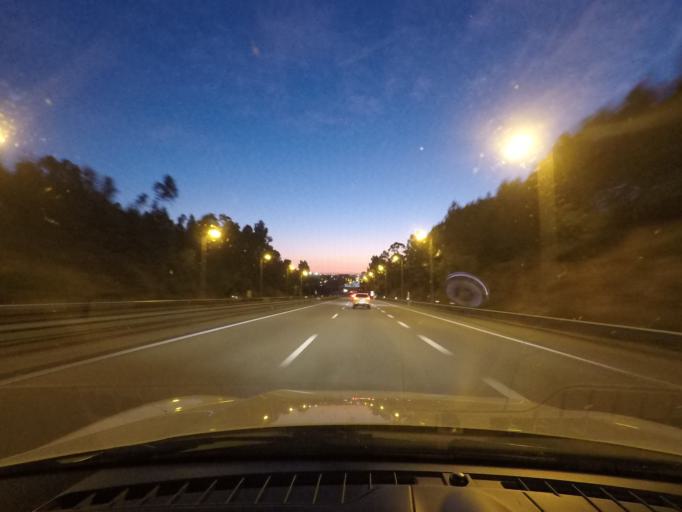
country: PT
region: Aveiro
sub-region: Santa Maria da Feira
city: Nogueira da Regedoura
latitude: 41.0085
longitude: -8.6078
